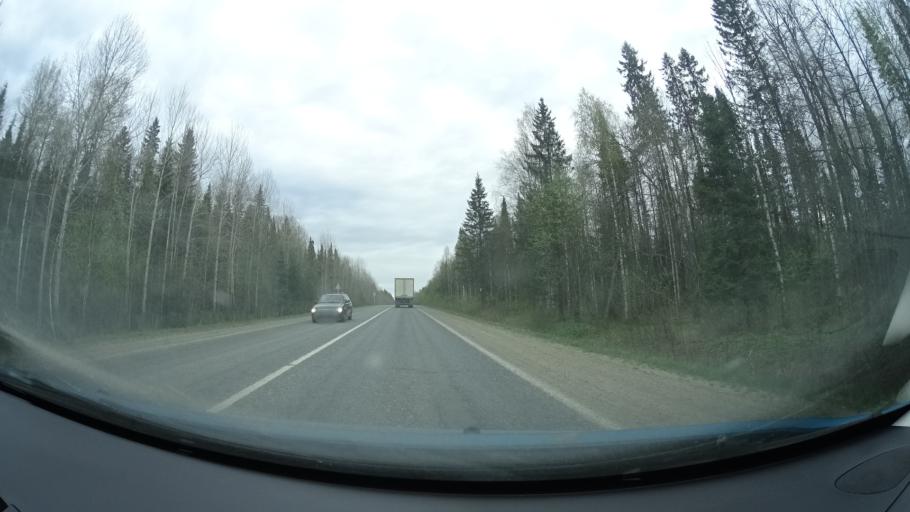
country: RU
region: Perm
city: Yugo-Kamskiy
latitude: 57.6116
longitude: 55.6377
